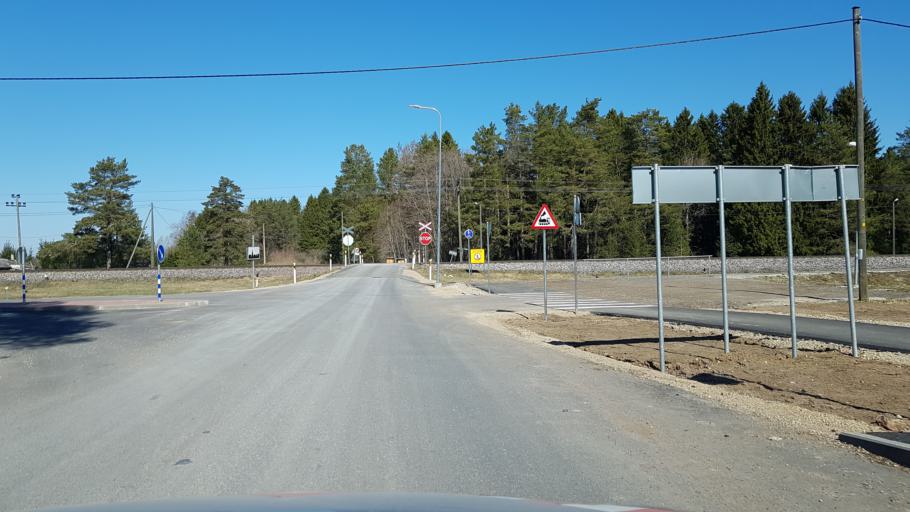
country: EE
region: Ida-Virumaa
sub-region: Kohtla-Nomme vald
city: Kohtla-Nomme
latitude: 59.3614
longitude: 27.1879
